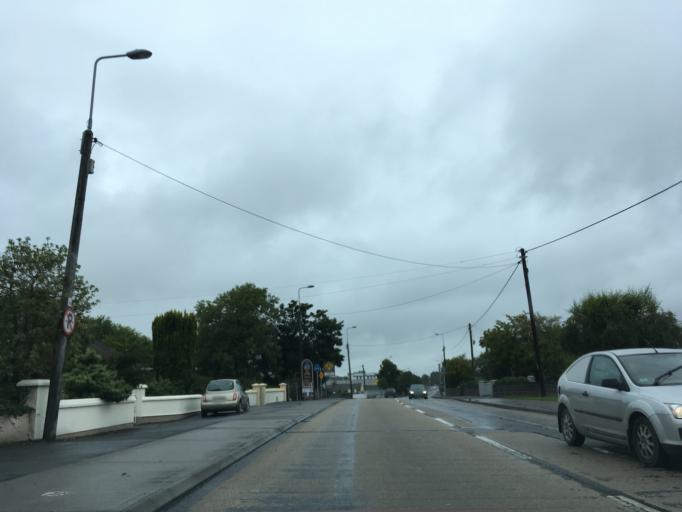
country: IE
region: Munster
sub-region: An Clar
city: Ennis
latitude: 52.8256
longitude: -8.9780
